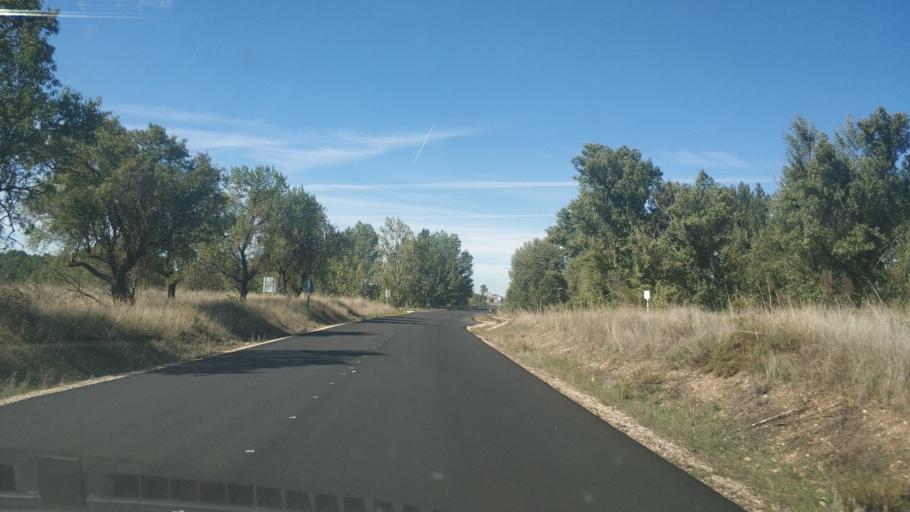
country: ES
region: Castille and Leon
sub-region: Provincia de Burgos
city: Puentedura
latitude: 42.0326
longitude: -3.6420
